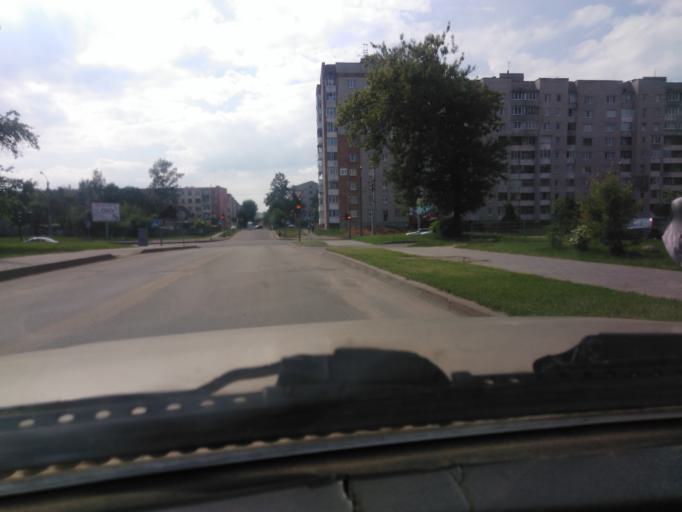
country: BY
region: Mogilev
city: Mahilyow
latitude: 53.9328
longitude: 30.3532
